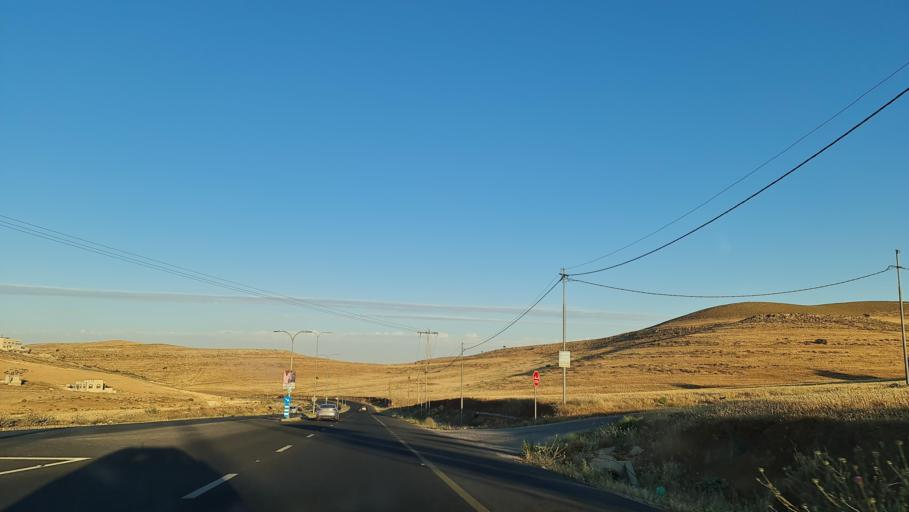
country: JO
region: Zarqa
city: Russeifa
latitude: 32.0858
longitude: 36.0009
